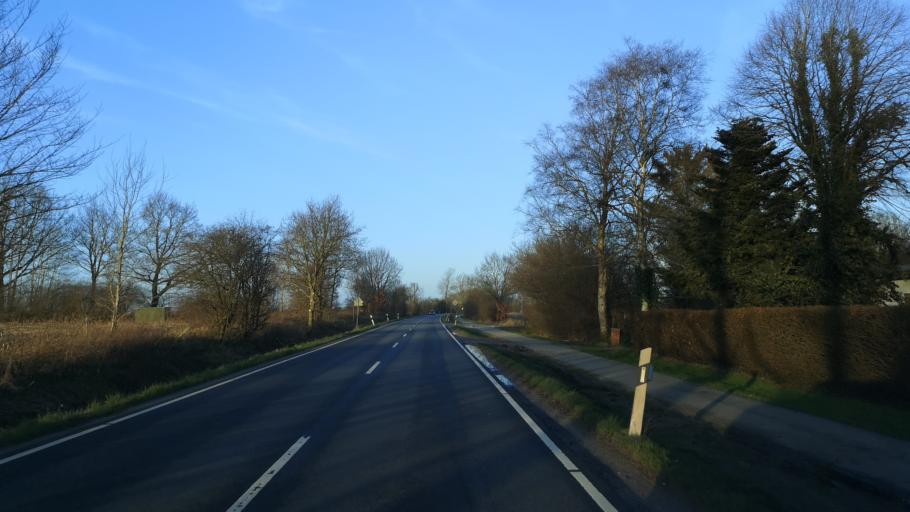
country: DE
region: Schleswig-Holstein
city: Grosssolt
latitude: 54.6856
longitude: 9.4929
